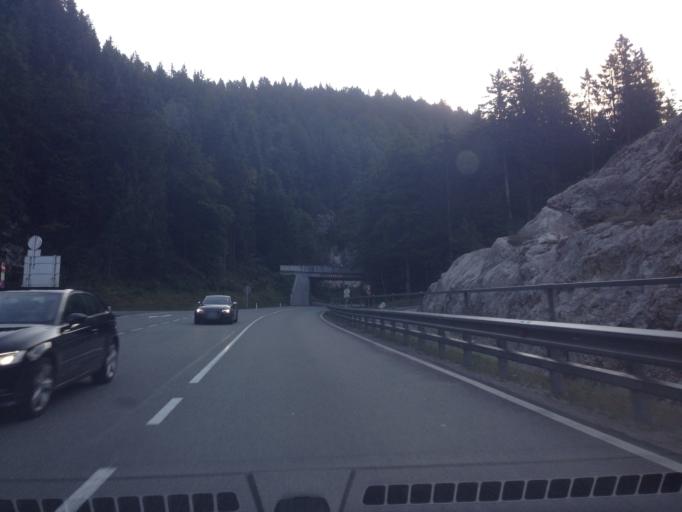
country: AT
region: Tyrol
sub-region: Politischer Bezirk Reutte
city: Ehenbichl
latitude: 47.4593
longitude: 10.7194
